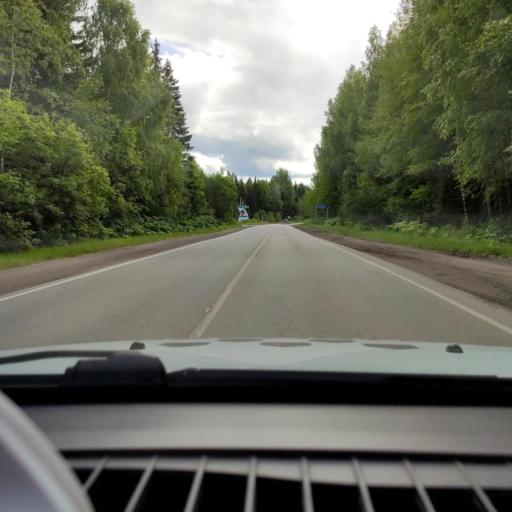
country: RU
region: Perm
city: Overyata
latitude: 58.1111
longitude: 55.8291
